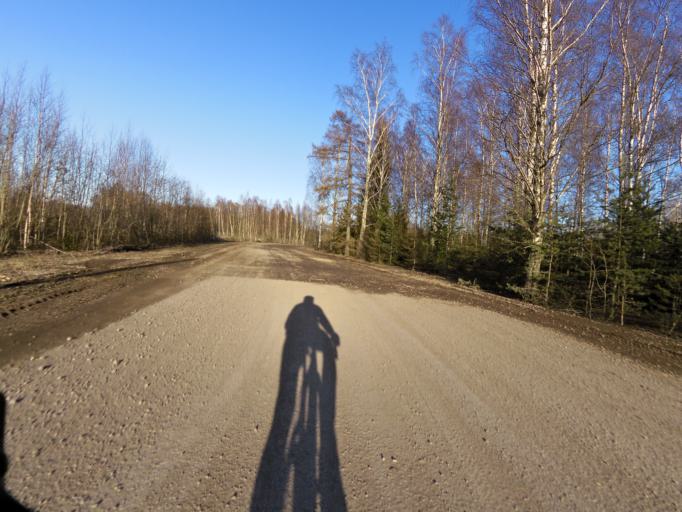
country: SE
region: Gaevleborg
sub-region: Gavle Kommun
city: Gavle
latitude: 60.6824
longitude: 17.2228
